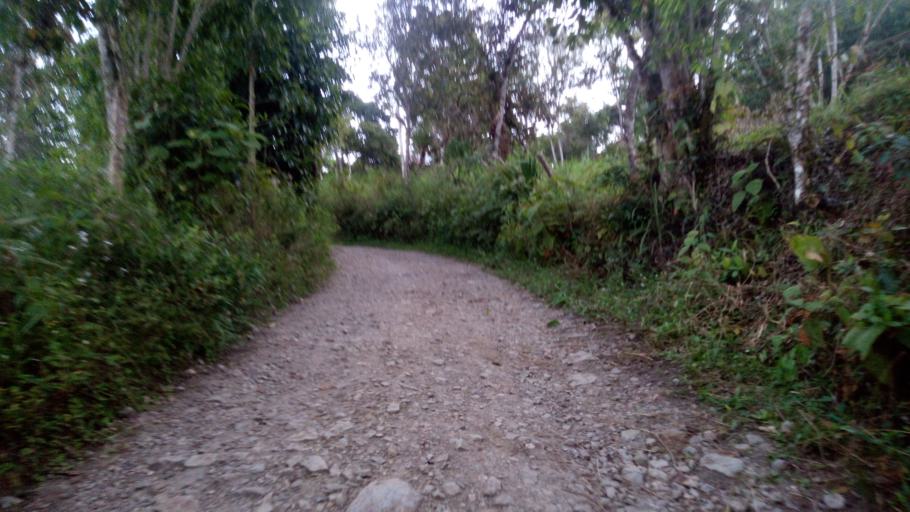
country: CO
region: Cundinamarca
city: Tenza
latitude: 5.0939
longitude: -73.4015
